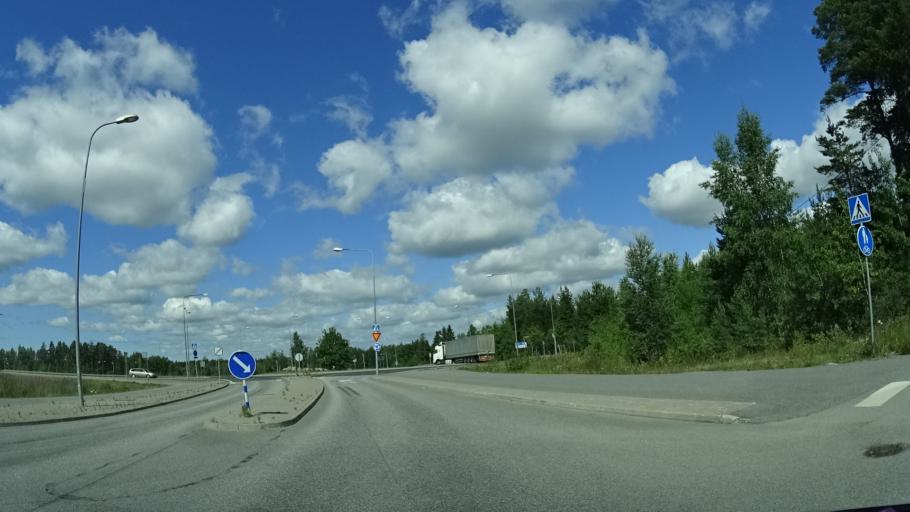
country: FI
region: Varsinais-Suomi
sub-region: Turku
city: Raisio
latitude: 60.5067
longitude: 22.1600
